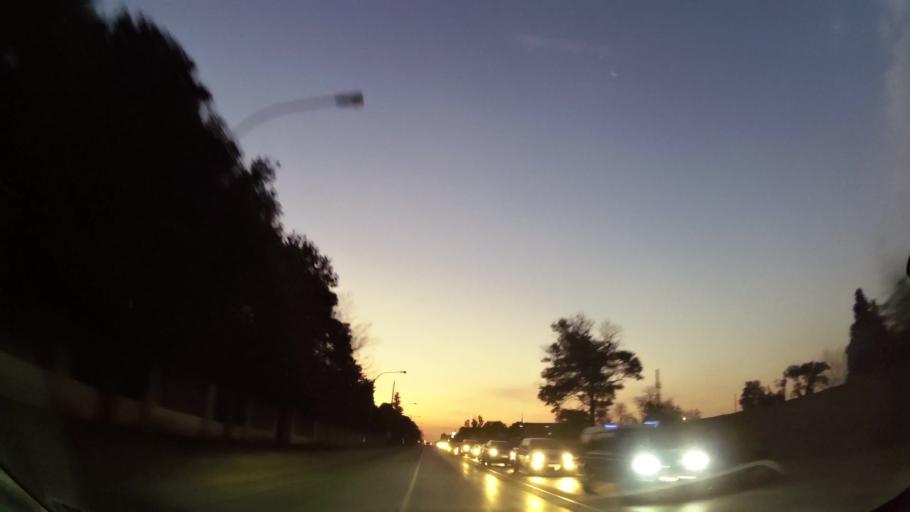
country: ZA
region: Gauteng
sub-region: Ekurhuleni Metropolitan Municipality
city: Benoni
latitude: -26.0968
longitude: 28.3108
